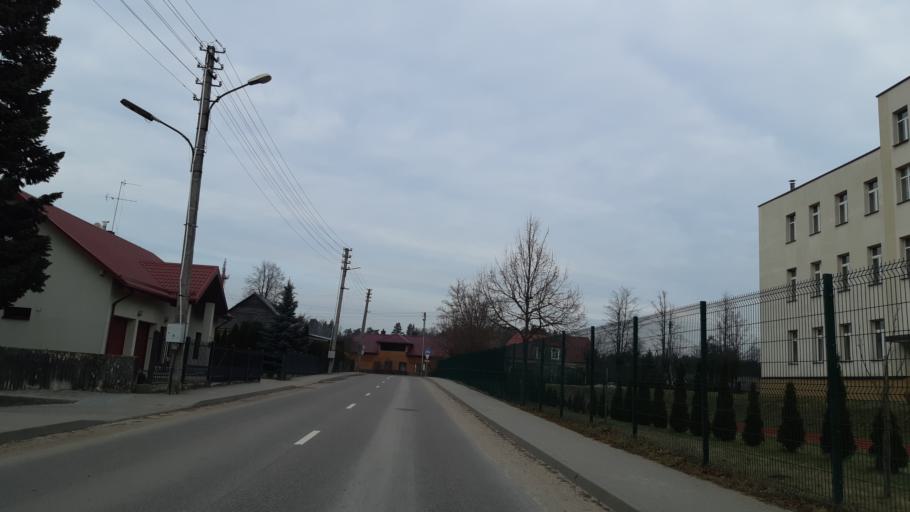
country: LT
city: Kazlu Ruda
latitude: 54.7532
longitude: 23.4957
